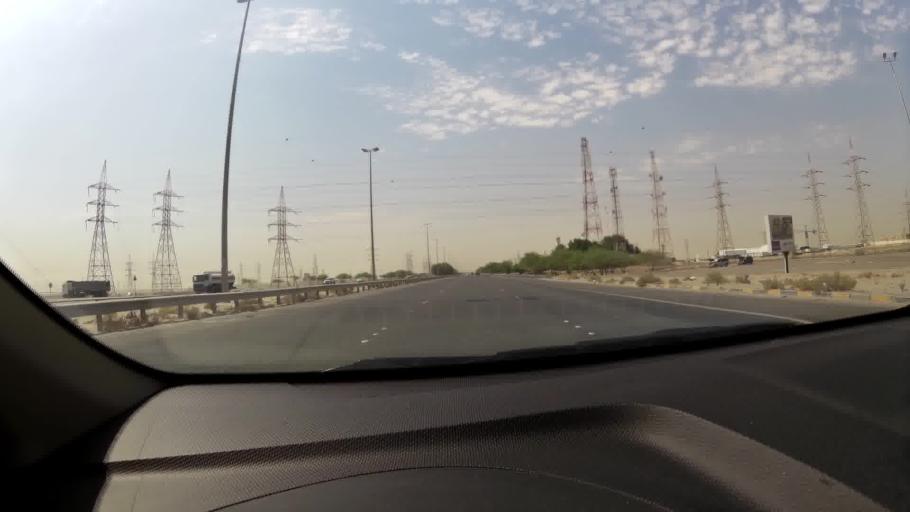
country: SA
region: Eastern Province
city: Al Khafji
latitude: 28.7353
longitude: 48.2851
